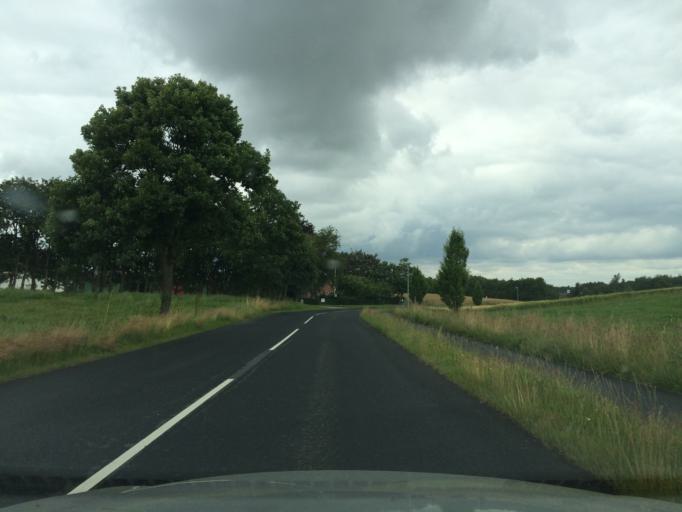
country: DK
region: Central Jutland
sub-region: Favrskov Kommune
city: Hammel
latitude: 56.2168
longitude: 9.7427
